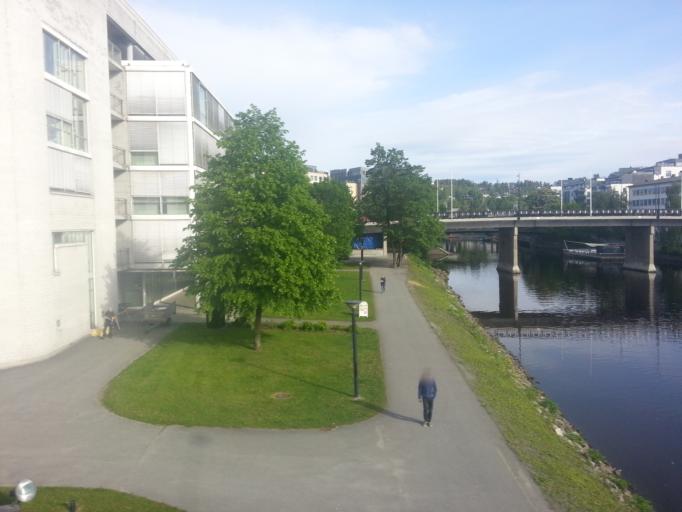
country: NO
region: Akershus
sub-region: Baerum
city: Sandvika
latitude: 59.8889
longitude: 10.5253
